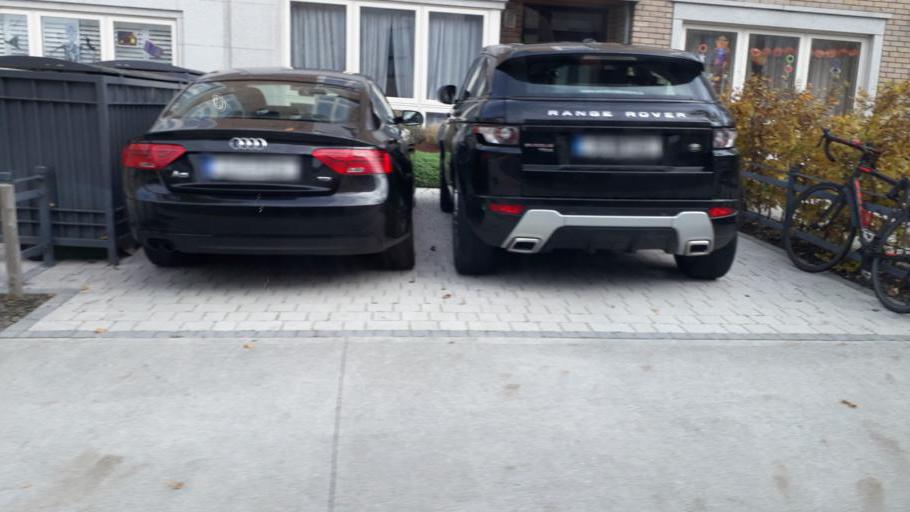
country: IE
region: Leinster
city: Mount Merrion
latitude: 53.2965
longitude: -6.2257
